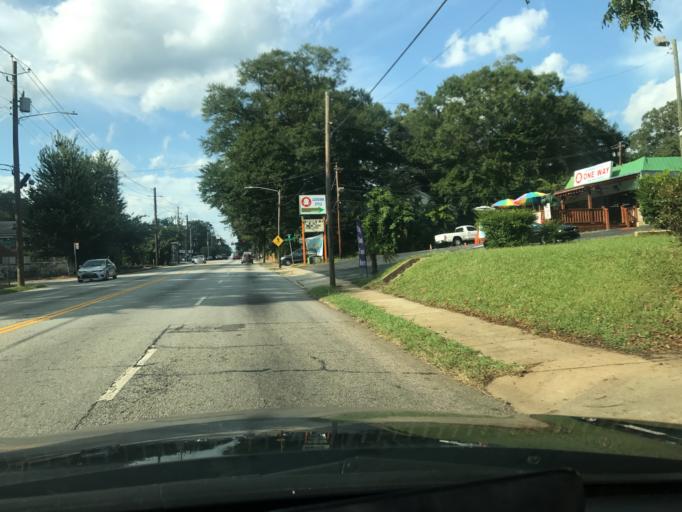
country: US
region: Georgia
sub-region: Fulton County
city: Atlanta
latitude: 33.7324
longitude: -84.3493
